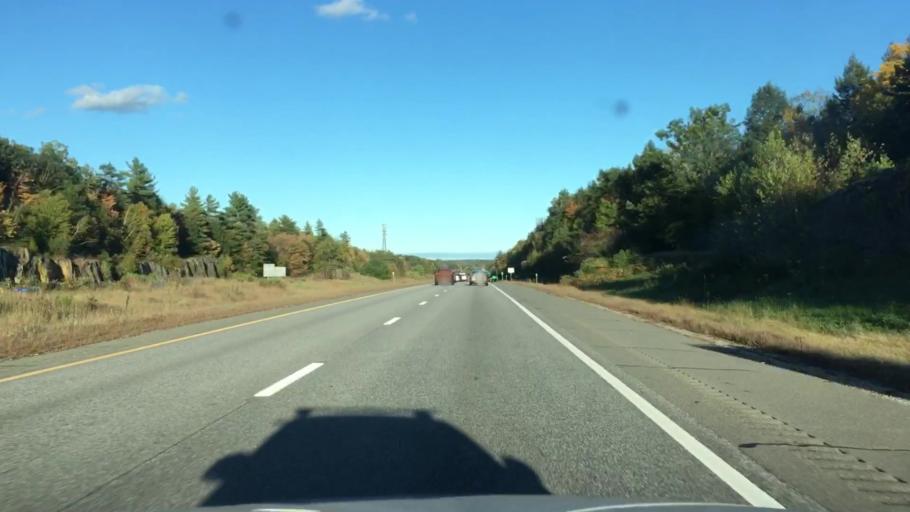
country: US
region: New Hampshire
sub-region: Rockingham County
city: Raymond
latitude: 43.0260
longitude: -71.1844
